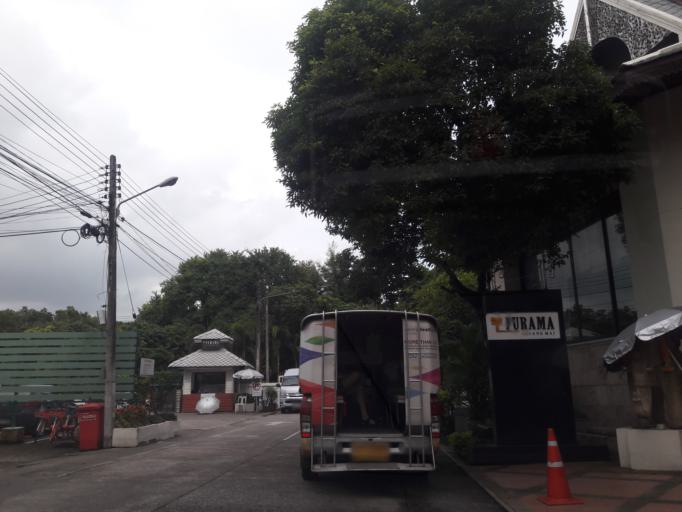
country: TH
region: Chiang Mai
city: Chiang Mai
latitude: 18.8023
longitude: 98.9709
